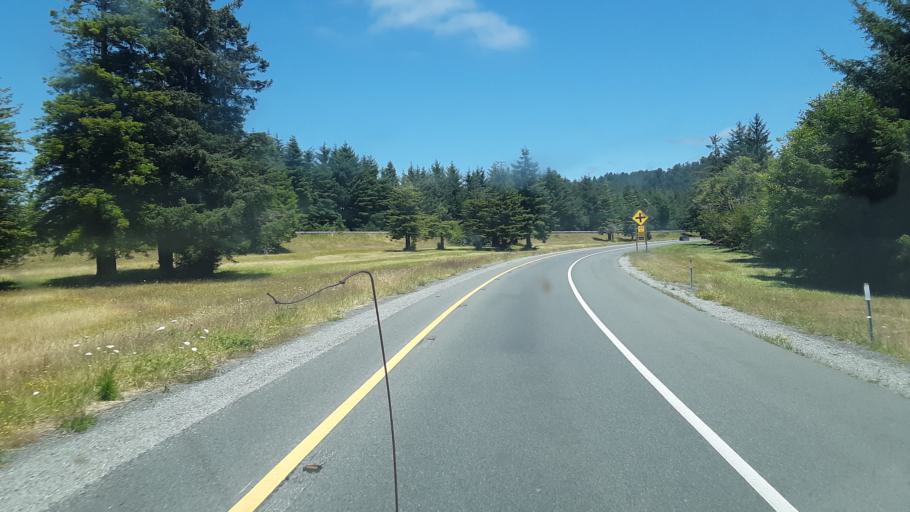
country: US
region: California
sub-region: Del Norte County
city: Bertsch-Oceanview
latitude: 41.8026
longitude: -124.1481
